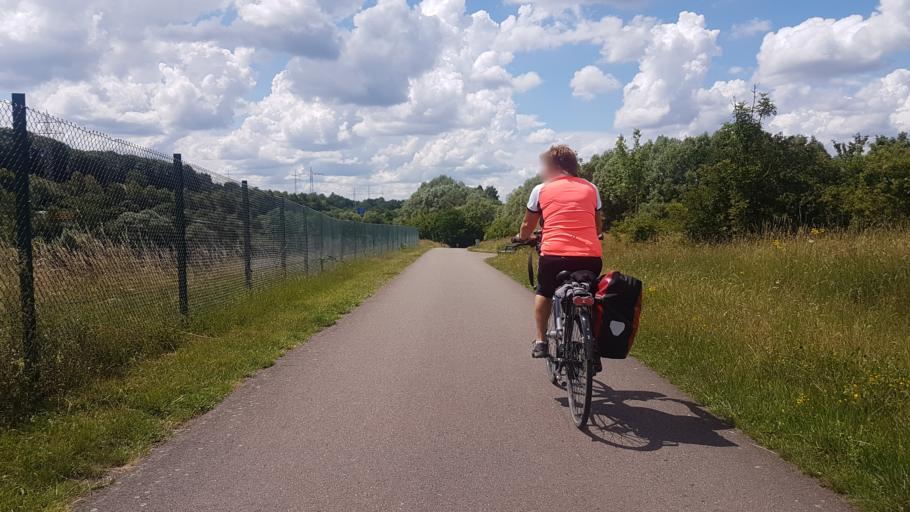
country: FR
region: Lorraine
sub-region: Departement de la Moselle
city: Schoeneck
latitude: 49.2421
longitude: 6.9255
